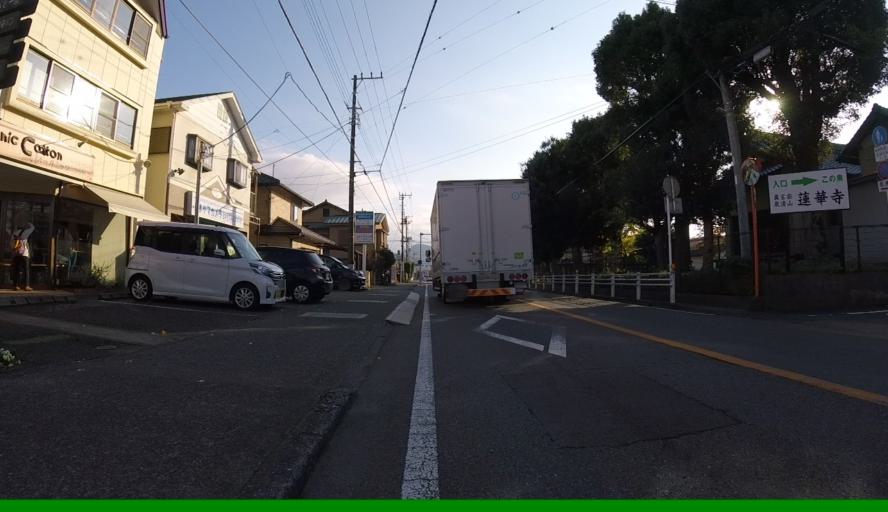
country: JP
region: Shizuoka
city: Mishima
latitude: 35.1012
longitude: 138.9044
